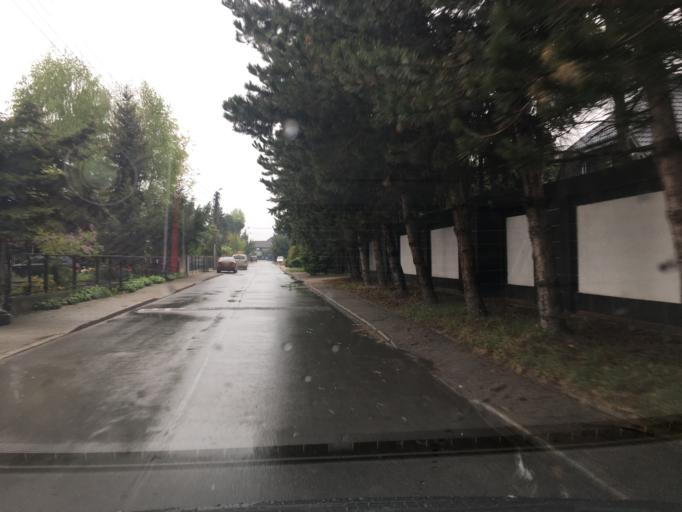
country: PL
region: Lower Silesian Voivodeship
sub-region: Powiat wroclawski
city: Zerniki Wroclawskie
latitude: 51.0292
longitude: 17.0606
